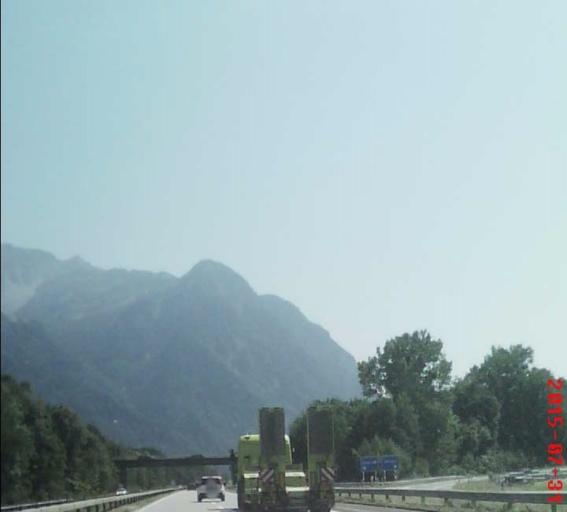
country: LI
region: Vaduz
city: Vaduz
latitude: 47.1318
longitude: 9.5091
